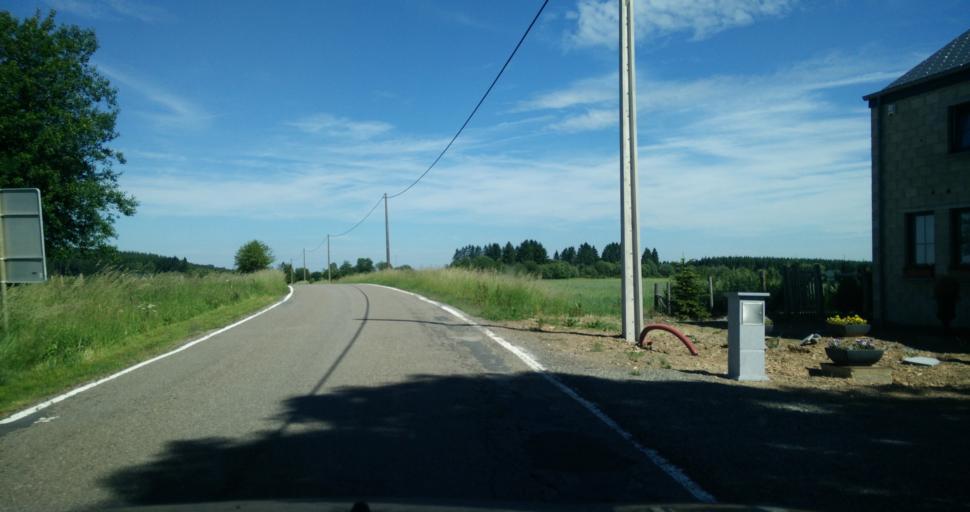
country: BE
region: Wallonia
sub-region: Province du Luxembourg
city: La Roche-en-Ardenne
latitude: 50.2132
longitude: 5.6346
